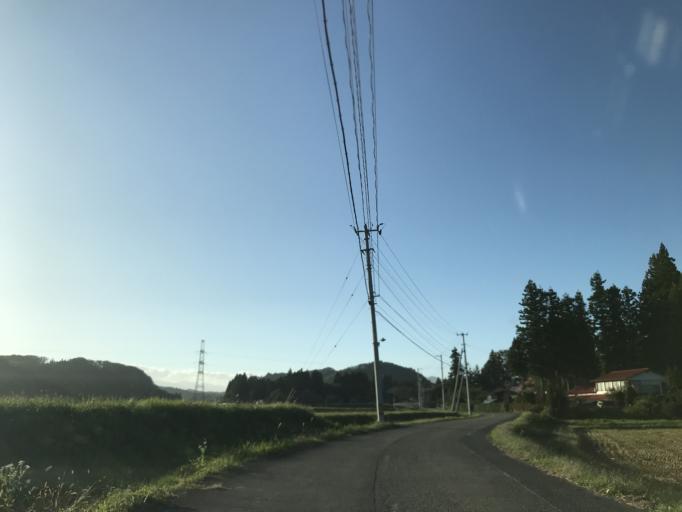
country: JP
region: Iwate
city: Ichinoseki
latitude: 38.9484
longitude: 141.0248
